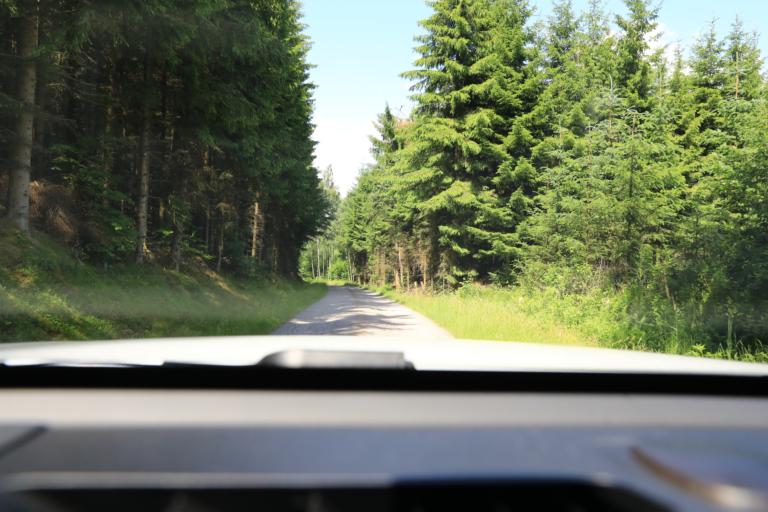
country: SE
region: Halland
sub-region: Varbergs Kommun
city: Tvaaker
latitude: 57.1026
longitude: 12.4763
